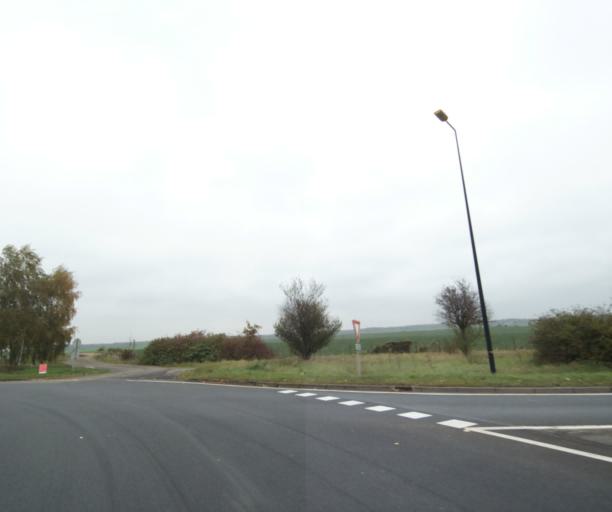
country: FR
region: Lorraine
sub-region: Departement de Meurthe-et-Moselle
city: Briey
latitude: 49.2552
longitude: 5.9485
